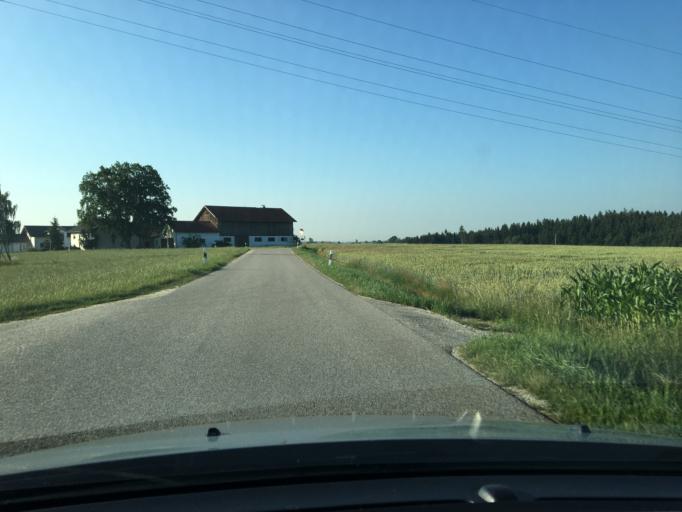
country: DE
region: Bavaria
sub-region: Lower Bavaria
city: Vilsbiburg
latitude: 48.4448
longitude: 12.3046
